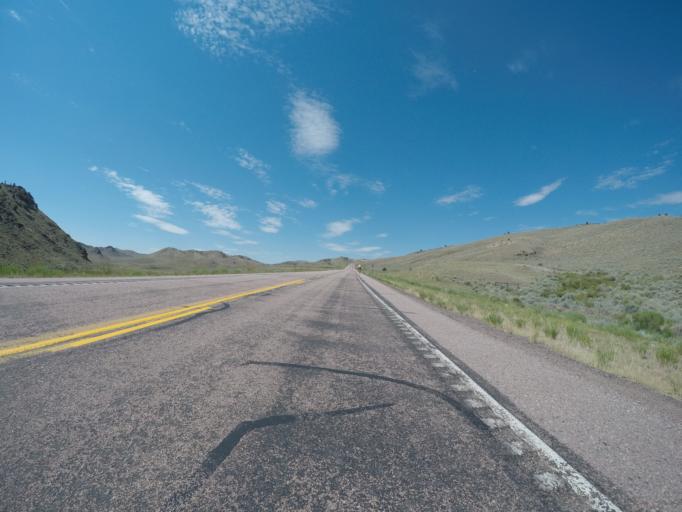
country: US
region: Wyoming
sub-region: Albany County
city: Laramie
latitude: 41.6925
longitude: -105.5096
